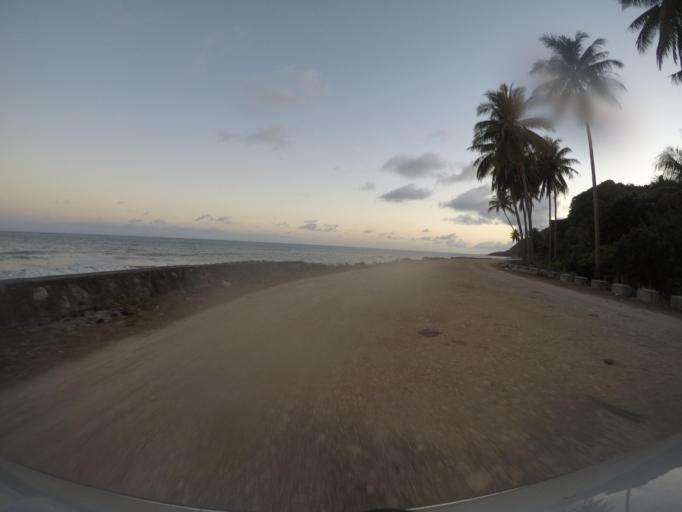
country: TL
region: Viqueque
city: Viqueque
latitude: -8.7849
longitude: 126.6359
